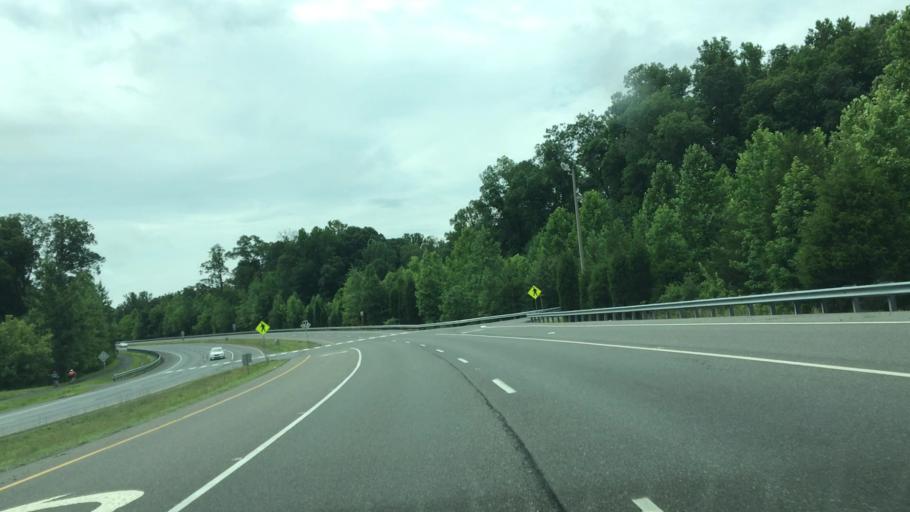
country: US
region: Virginia
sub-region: Prince William County
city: Buckhall
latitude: 38.7016
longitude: -77.4081
